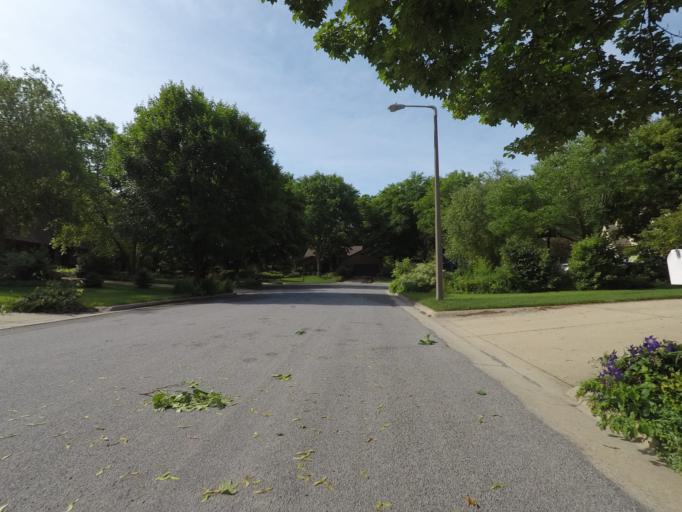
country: US
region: Wisconsin
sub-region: Dane County
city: Middleton
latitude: 43.0769
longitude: -89.4956
